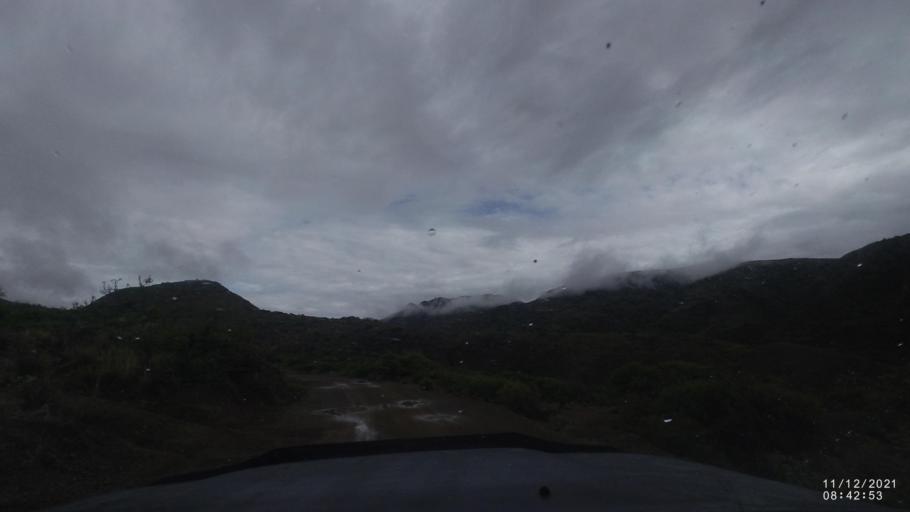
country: BO
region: Cochabamba
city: Tarata
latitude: -17.9150
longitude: -65.9356
